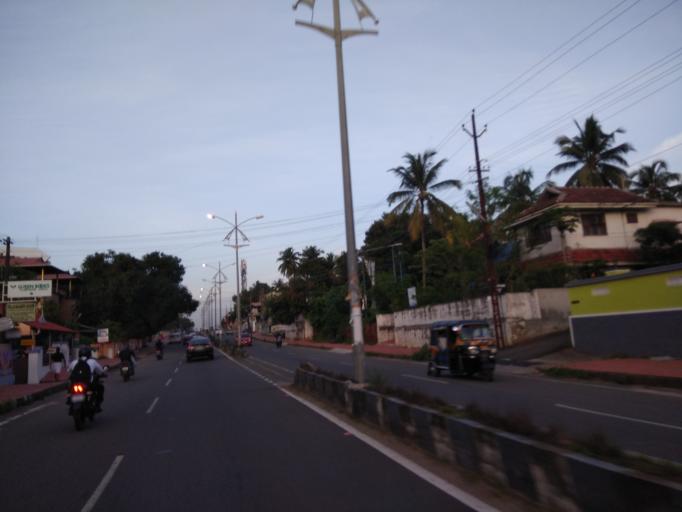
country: IN
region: Kerala
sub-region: Thrissur District
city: Trichur
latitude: 10.5213
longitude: 76.1945
